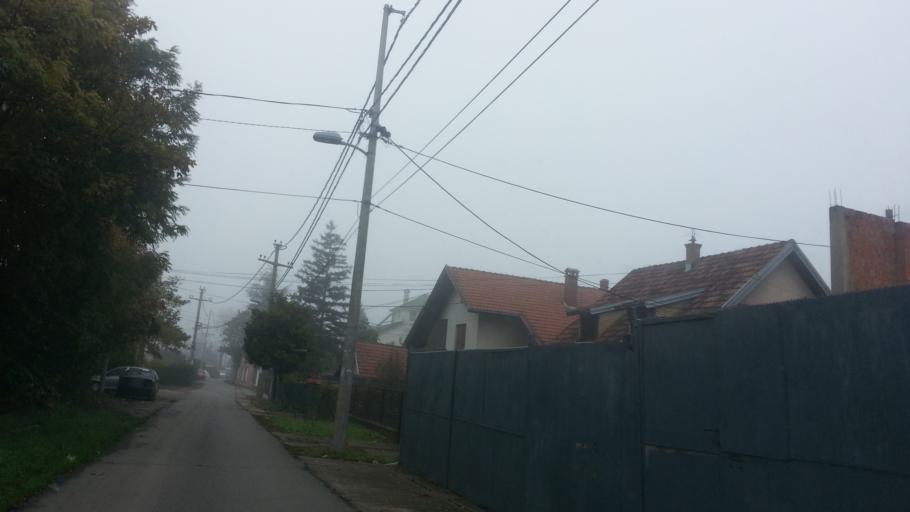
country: RS
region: Central Serbia
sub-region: Belgrade
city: Zemun
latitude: 44.8598
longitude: 20.3812
